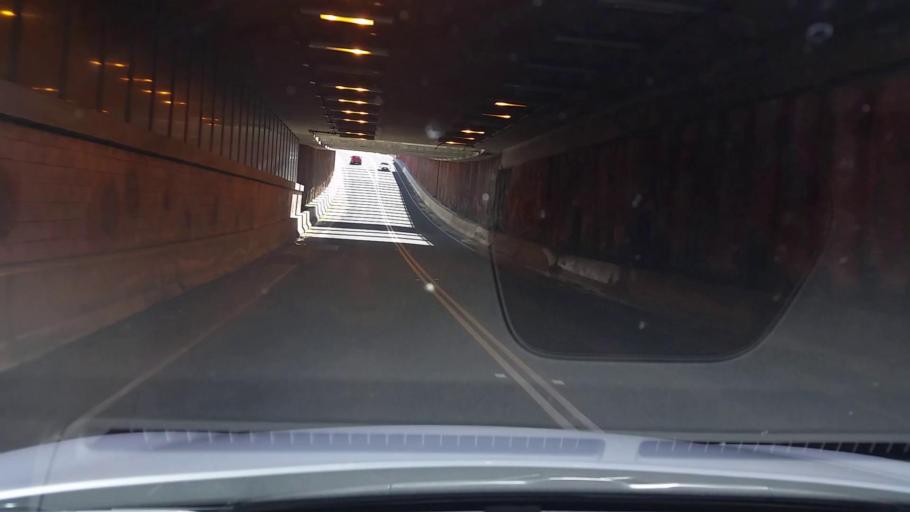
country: AU
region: Victoria
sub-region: Mornington Peninsula
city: Safety Beach
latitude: -38.3066
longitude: 144.9946
